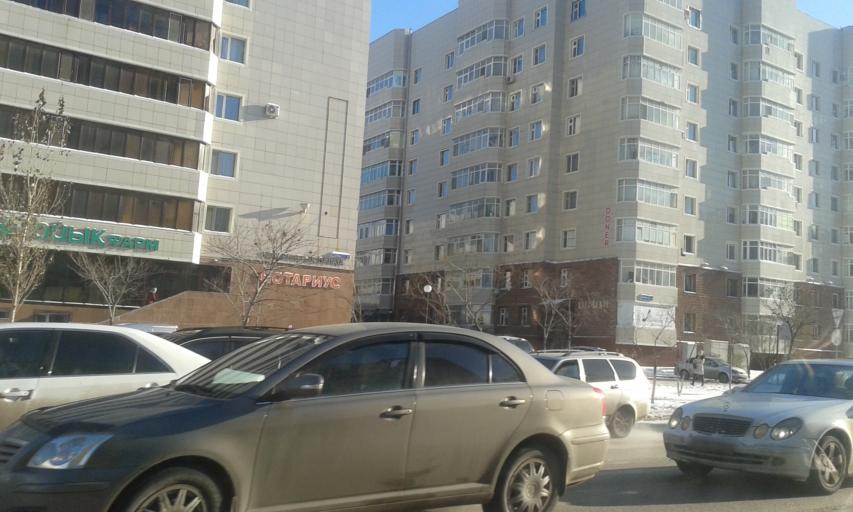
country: KZ
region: Astana Qalasy
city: Astana
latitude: 51.1262
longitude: 71.4238
